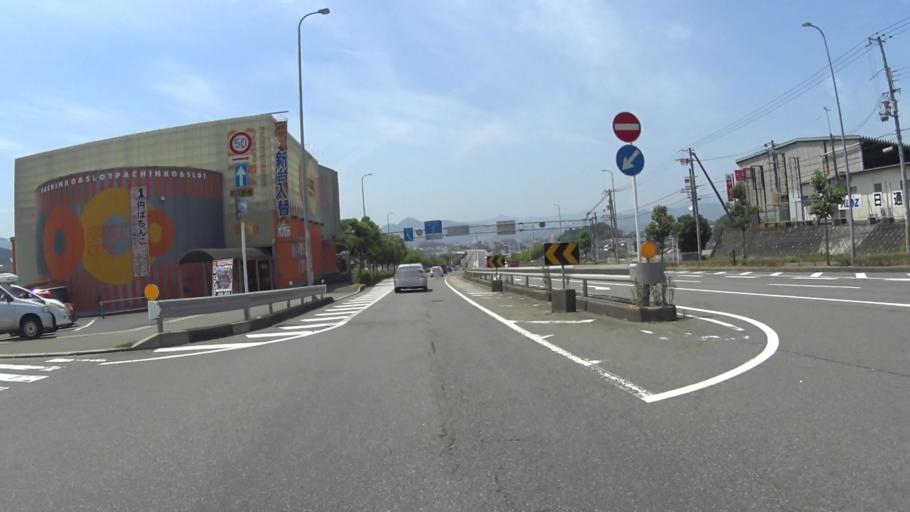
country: JP
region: Kyoto
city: Fukuchiyama
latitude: 35.2876
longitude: 135.1517
